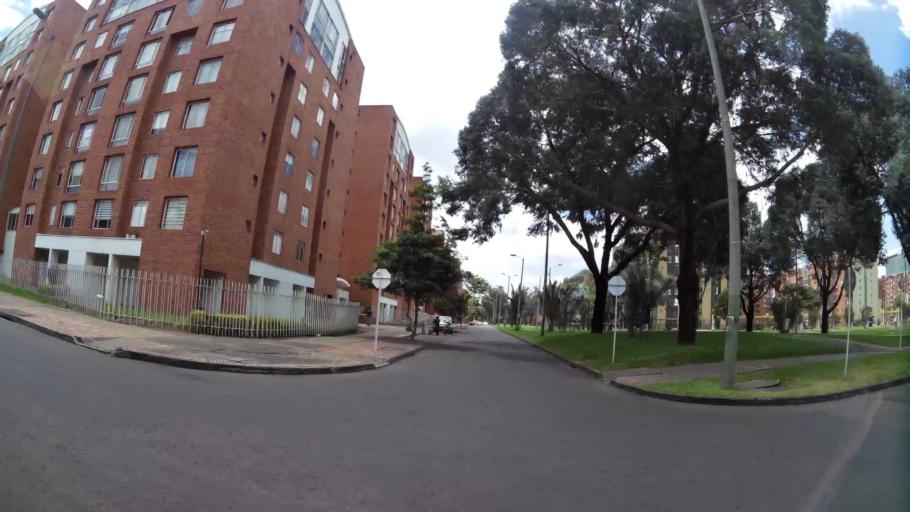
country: CO
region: Bogota D.C.
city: Bogota
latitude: 4.6400
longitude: -74.1007
